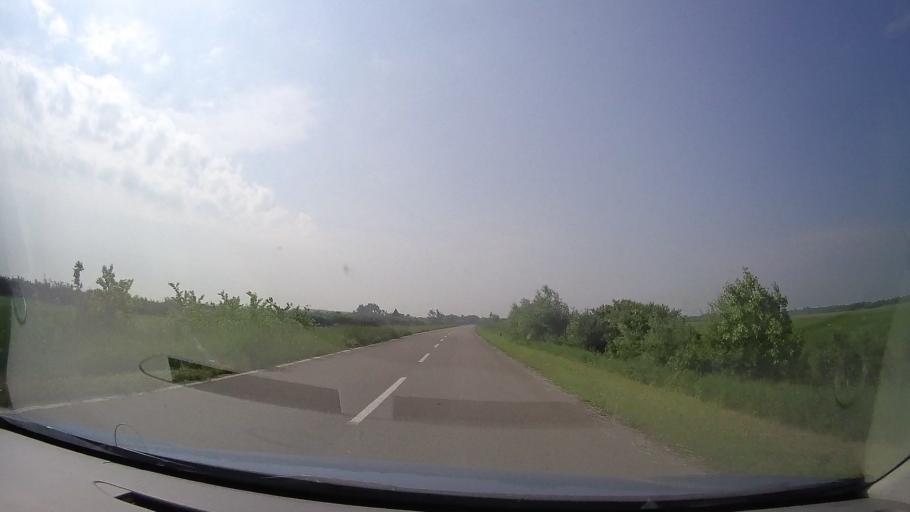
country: RS
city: Jasa Tomic
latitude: 45.4609
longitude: 20.8537
